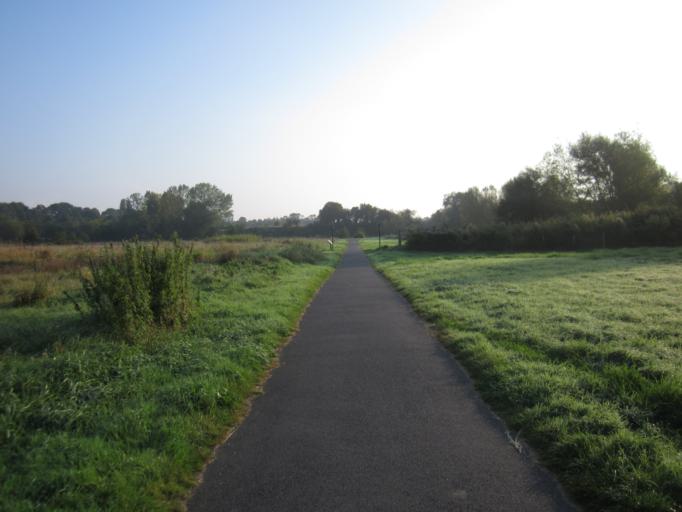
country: GB
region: England
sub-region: Kent
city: Canterbury
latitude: 51.2726
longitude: 1.0589
